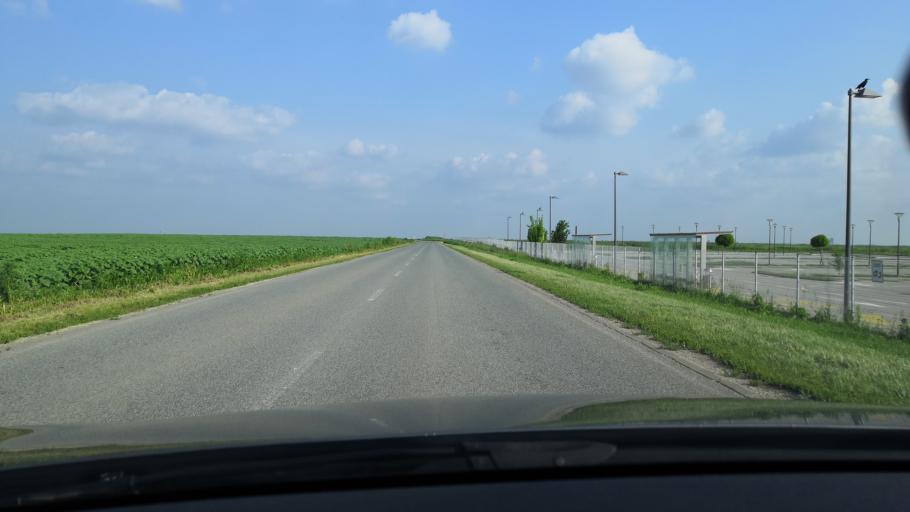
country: RS
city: Beska
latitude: 45.0936
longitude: 20.0957
